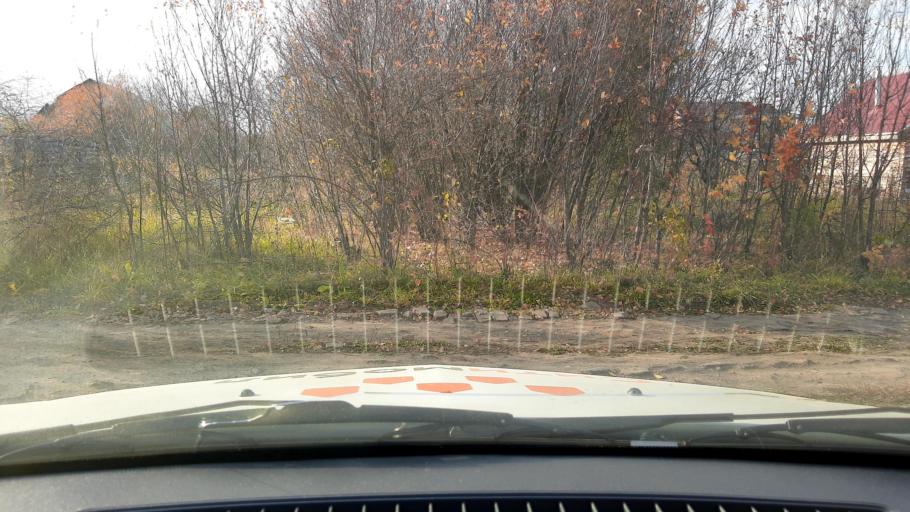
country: RU
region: Bashkortostan
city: Kabakovo
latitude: 54.7119
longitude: 56.1742
